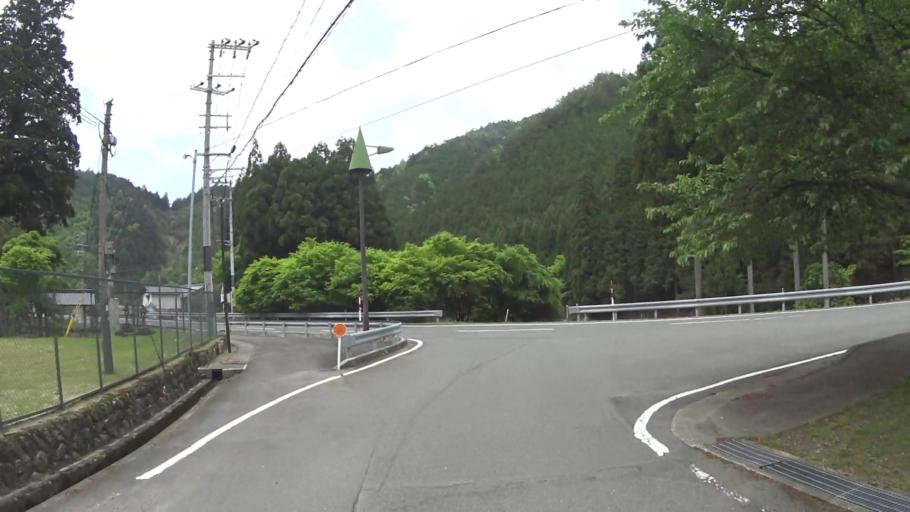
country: JP
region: Kyoto
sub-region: Kyoto-shi
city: Kamigyo-ku
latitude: 35.2079
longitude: 135.7402
